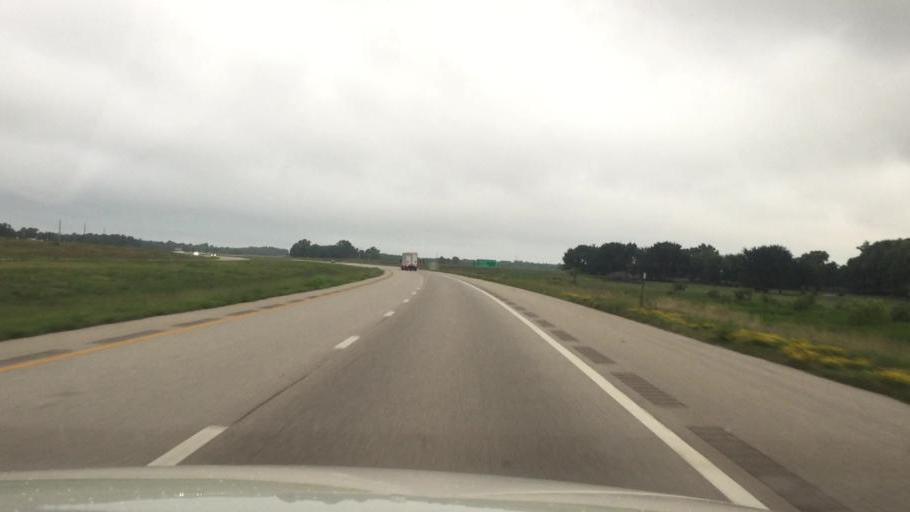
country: US
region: Kansas
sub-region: Montgomery County
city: Coffeyville
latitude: 37.0784
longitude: -95.5897
